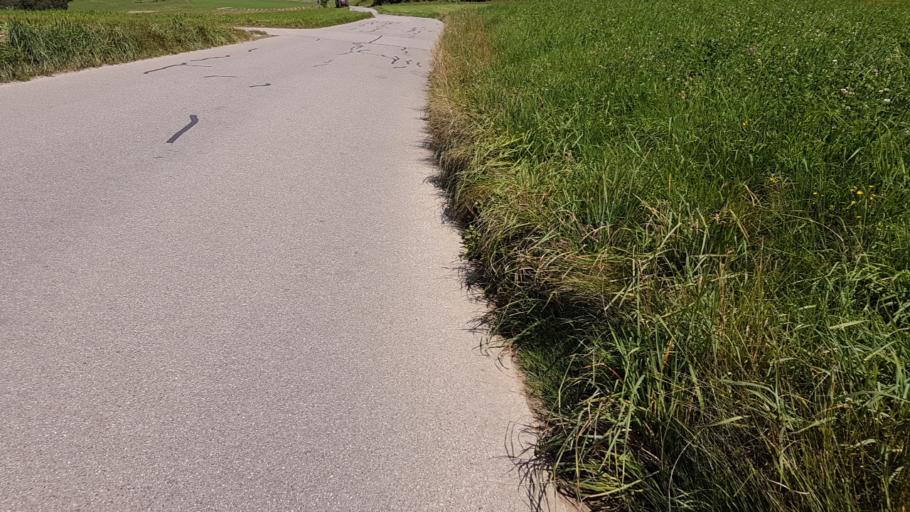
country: CH
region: Bern
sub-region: Bern-Mittelland District
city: Konolfingen
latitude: 46.8597
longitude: 7.6255
